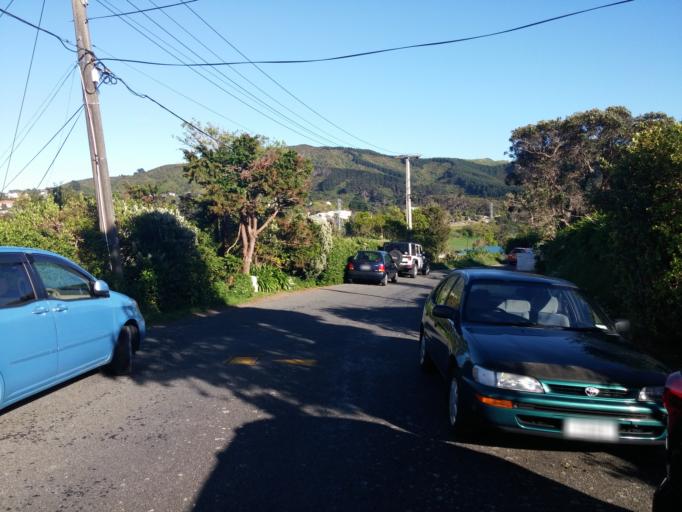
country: NZ
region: Wellington
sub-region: Wellington City
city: Kelburn
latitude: -41.2804
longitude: 174.7575
